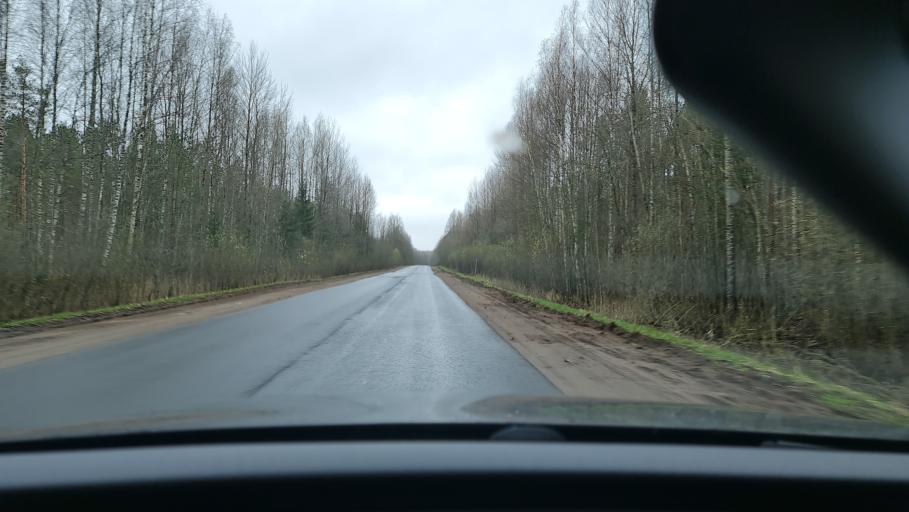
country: RU
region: Novgorod
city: Demyansk
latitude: 57.6834
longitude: 32.5586
